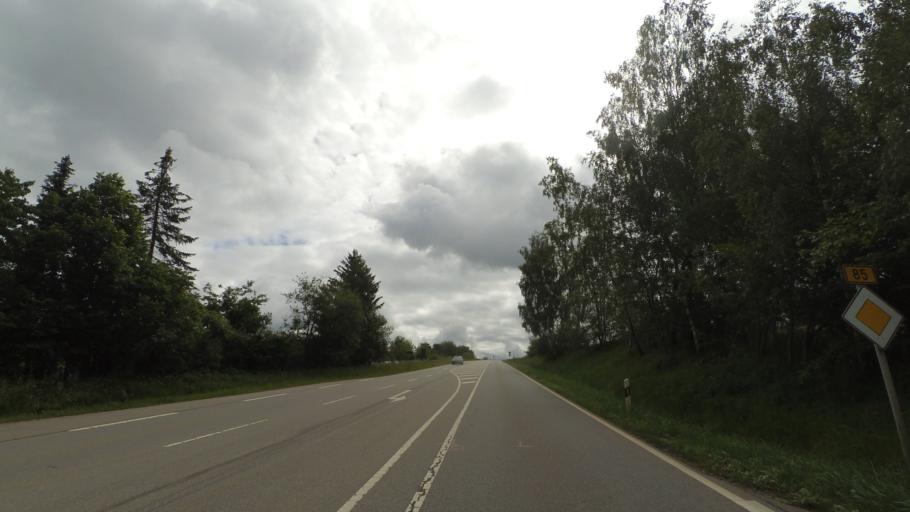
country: DE
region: Bavaria
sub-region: Lower Bavaria
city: Prackenbach
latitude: 49.0919
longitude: 12.8279
